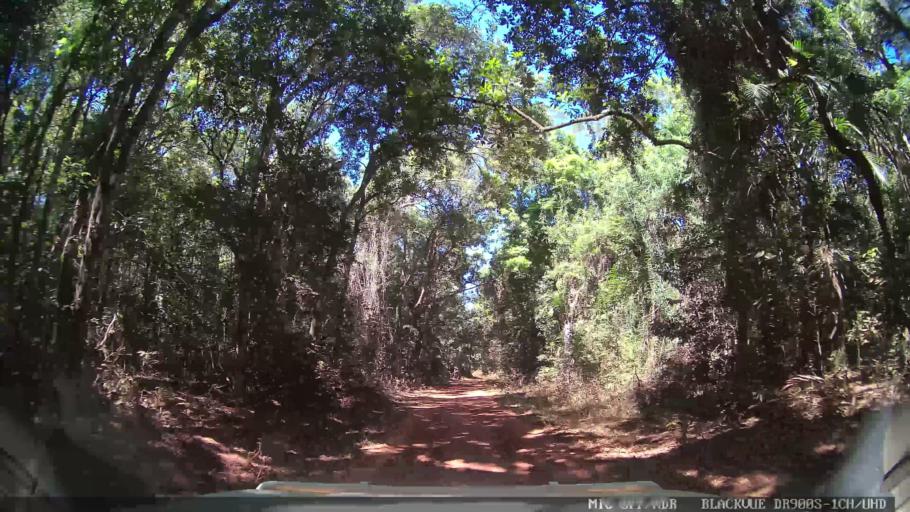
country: AU
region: Queensland
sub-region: Torres
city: Thursday Island
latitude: -10.7694
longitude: 142.5368
